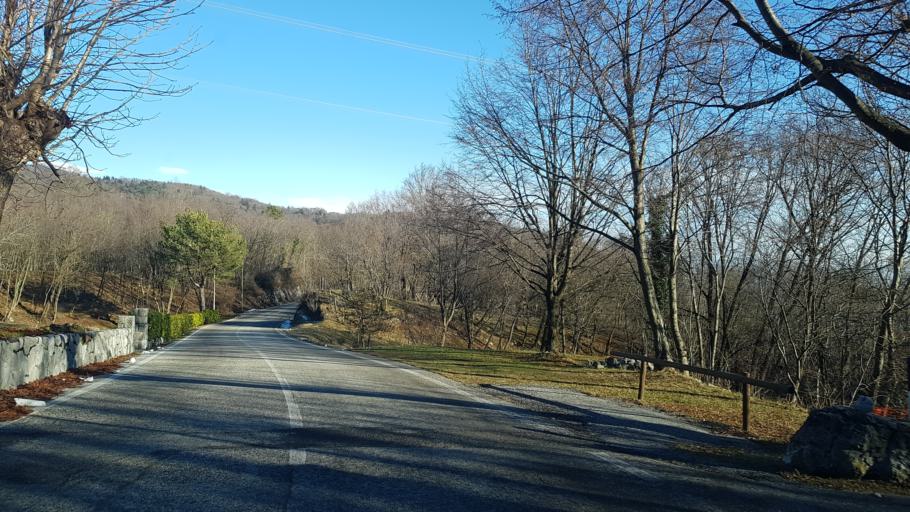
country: IT
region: Friuli Venezia Giulia
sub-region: Provincia di Udine
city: Forgaria nel Friuli
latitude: 46.2339
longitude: 12.9899
